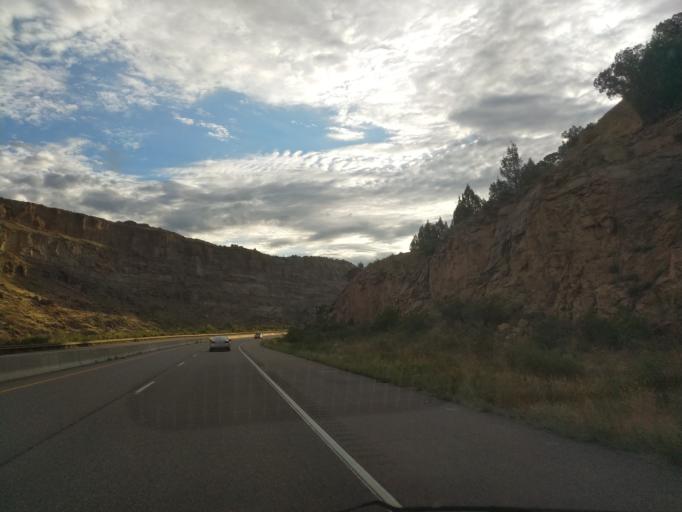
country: US
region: Colorado
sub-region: Mesa County
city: Palisade
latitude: 39.2359
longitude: -108.2702
